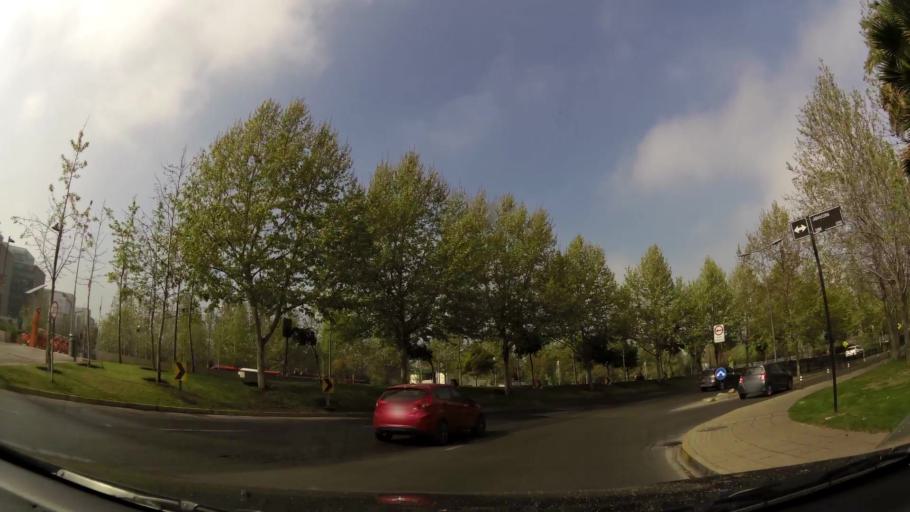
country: CL
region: Santiago Metropolitan
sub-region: Provincia de Santiago
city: Villa Presidente Frei, Nunoa, Santiago, Chile
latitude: -33.3839
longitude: -70.5347
